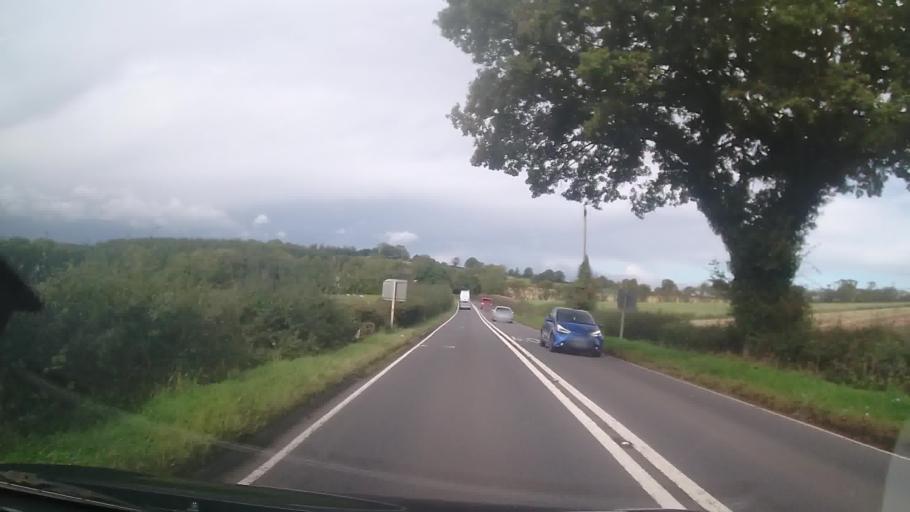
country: GB
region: England
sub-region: Shropshire
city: Romsley
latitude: 52.4323
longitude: -2.3139
